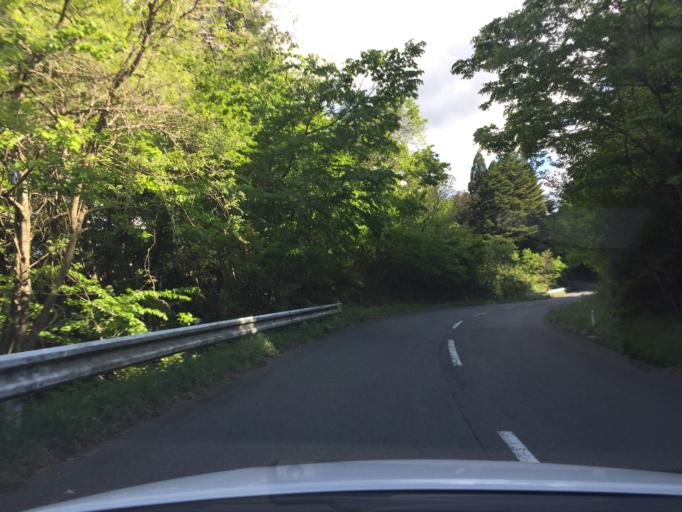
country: JP
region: Miyagi
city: Marumori
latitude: 37.7330
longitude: 140.8029
